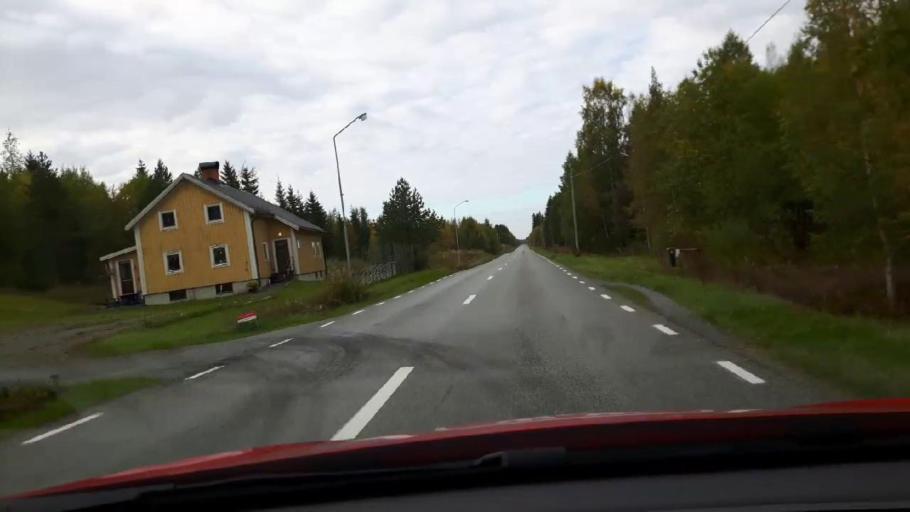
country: SE
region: Jaemtland
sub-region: Krokoms Kommun
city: Krokom
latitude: 63.1854
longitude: 14.0718
